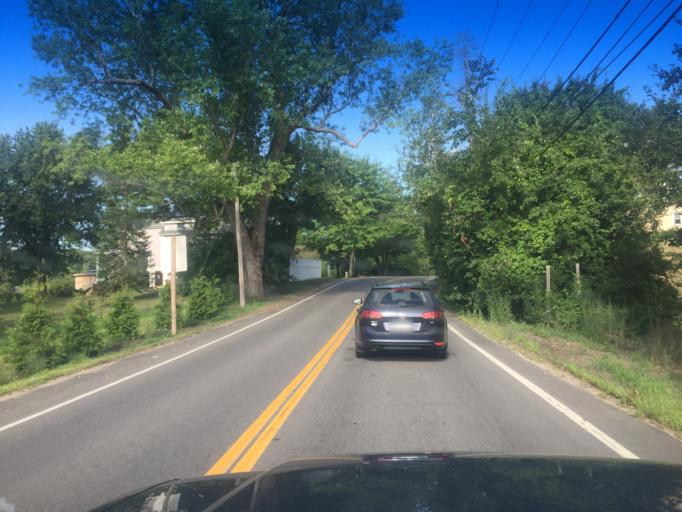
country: US
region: Maine
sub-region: York County
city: South Berwick
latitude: 43.2120
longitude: -70.7877
